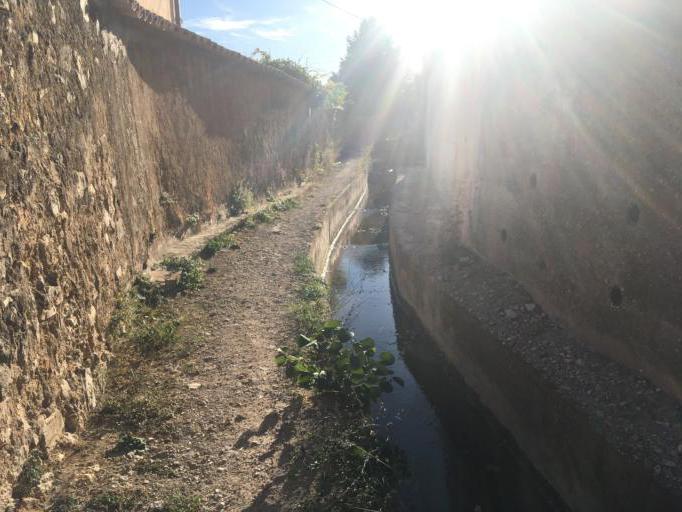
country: FR
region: Provence-Alpes-Cote d'Azur
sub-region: Departement du Var
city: Draguignan
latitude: 43.5438
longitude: 6.4576
